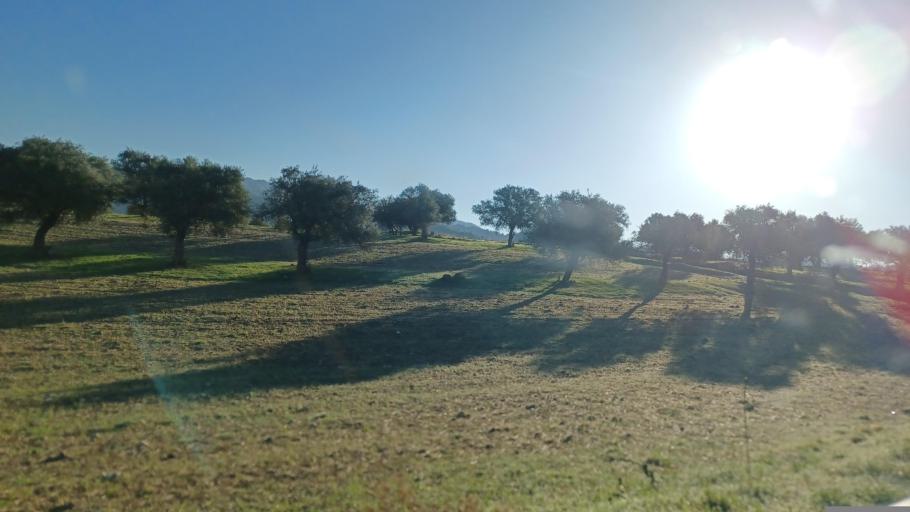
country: CY
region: Pafos
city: Polis
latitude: 34.9549
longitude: 32.5457
